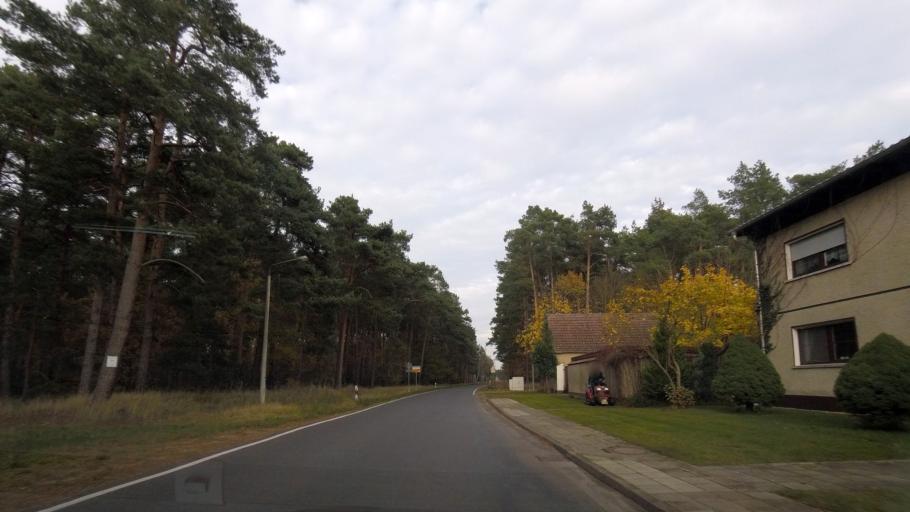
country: DE
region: Brandenburg
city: Borkheide
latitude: 52.1694
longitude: 12.8549
